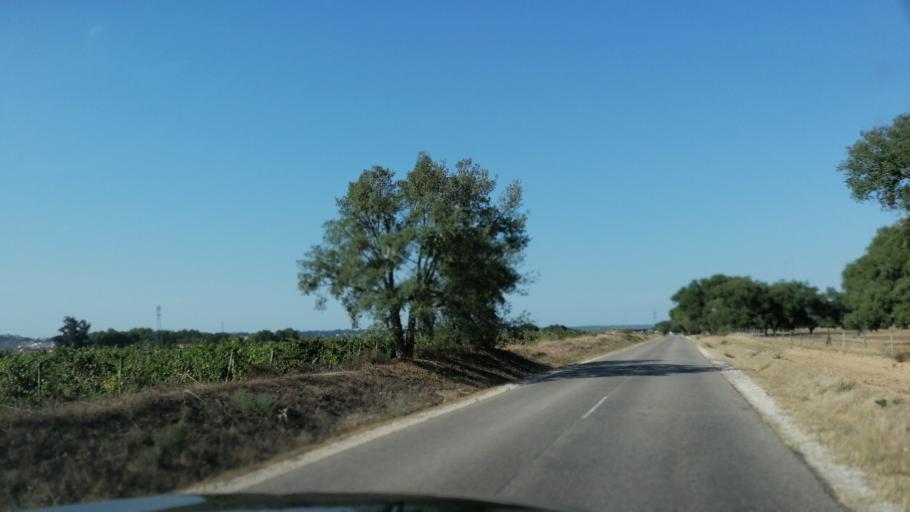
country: PT
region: Santarem
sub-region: Coruche
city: Coruche
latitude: 38.9303
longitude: -8.5205
